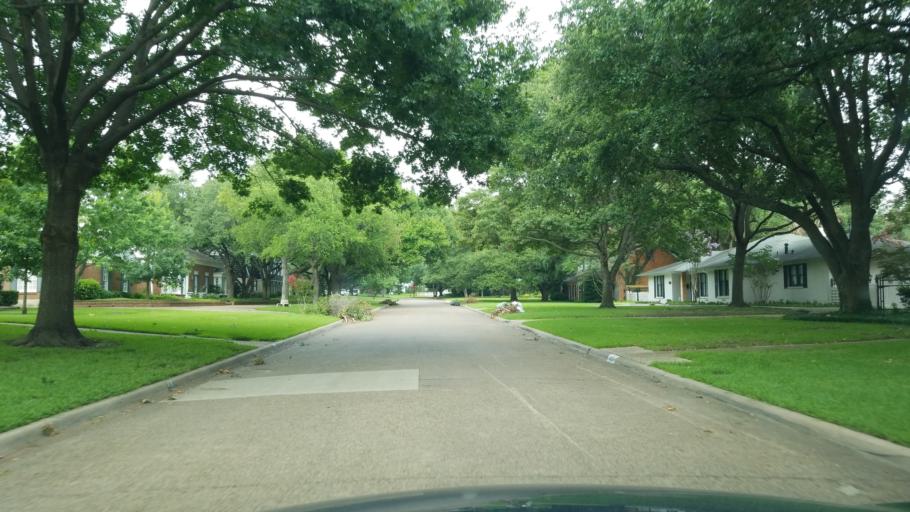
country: US
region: Texas
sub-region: Dallas County
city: University Park
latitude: 32.8982
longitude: -96.8360
